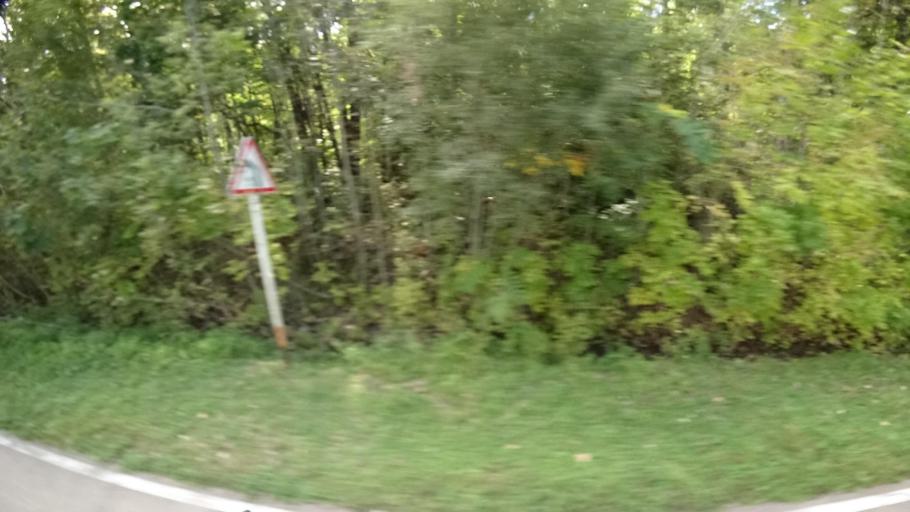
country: RU
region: Primorskiy
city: Yakovlevka
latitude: 44.4017
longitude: 133.5960
